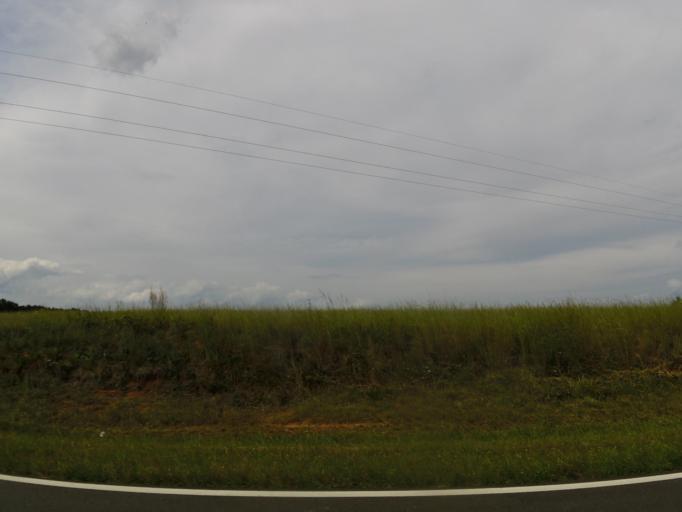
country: US
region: Georgia
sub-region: McDuffie County
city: Thomson
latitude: 33.5286
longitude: -82.4779
